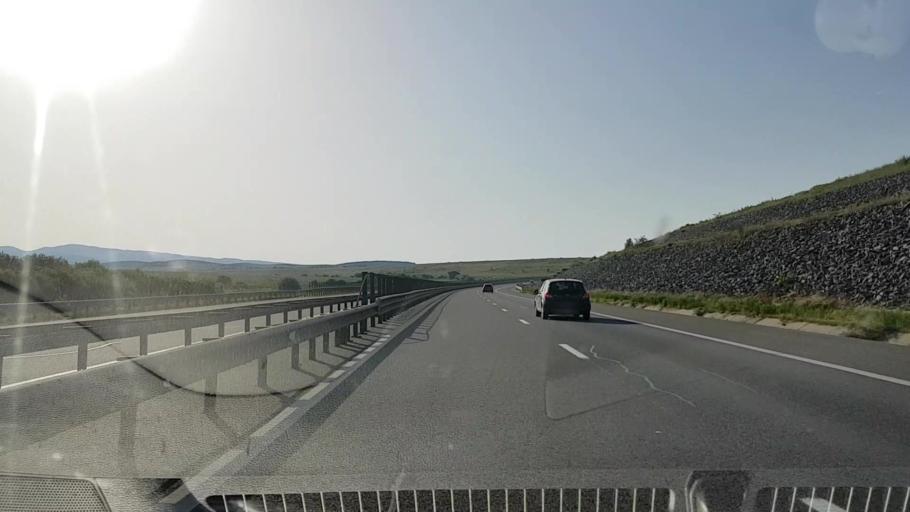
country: RO
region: Cluj
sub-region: Comuna Ciurila
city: Ciurila
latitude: 46.6426
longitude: 23.5226
